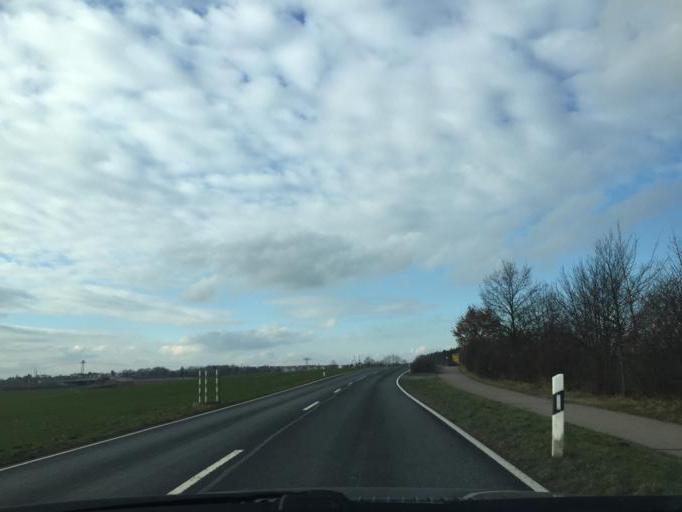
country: DE
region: Saxony
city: Radeburg
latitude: 51.2102
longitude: 13.7473
